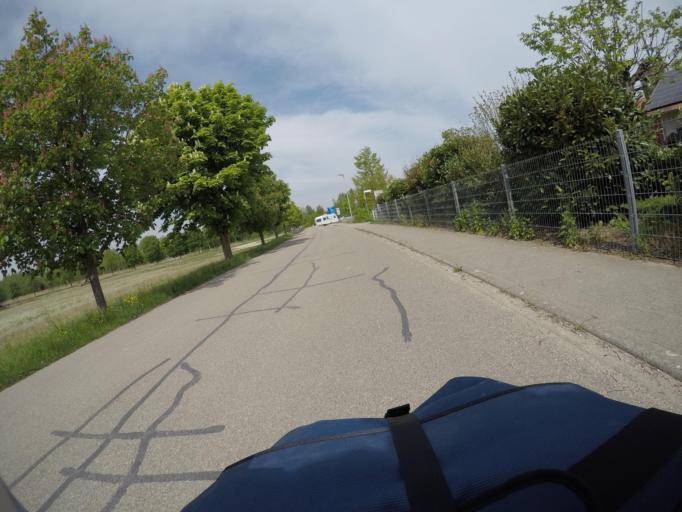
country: DE
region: Baden-Wuerttemberg
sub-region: Karlsruhe Region
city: Schwarzach
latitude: 48.7718
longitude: 8.0426
